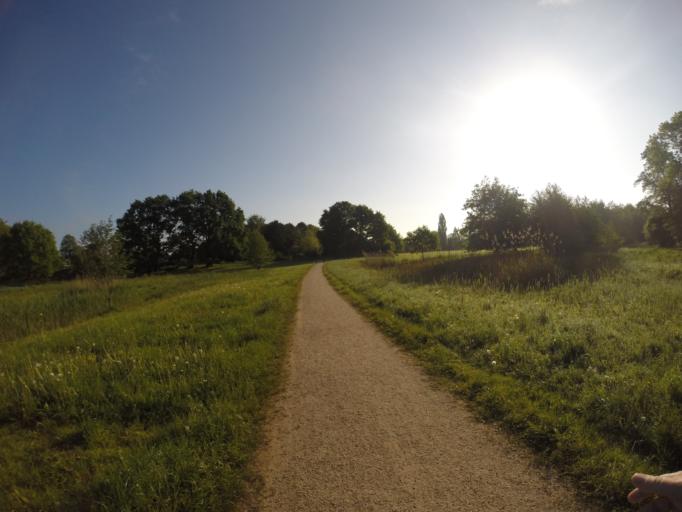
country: NL
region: Gelderland
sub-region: Oude IJsselstreek
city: Gendringen
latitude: 51.9239
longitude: 6.3552
